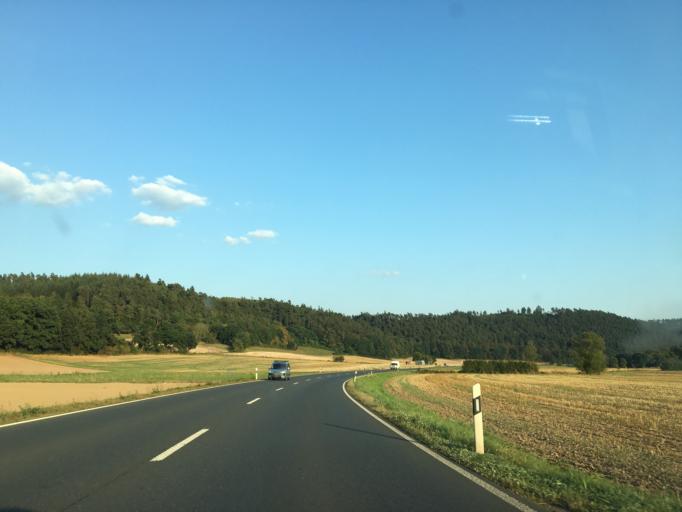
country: DE
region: Hesse
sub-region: Regierungsbezirk Giessen
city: Colbe
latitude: 50.8734
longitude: 8.7807
